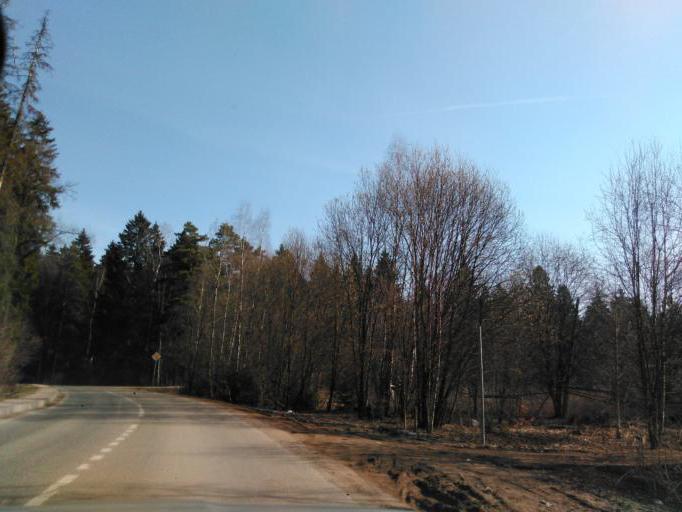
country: RU
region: Moskovskaya
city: Skhodnya
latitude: 55.8900
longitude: 37.2680
